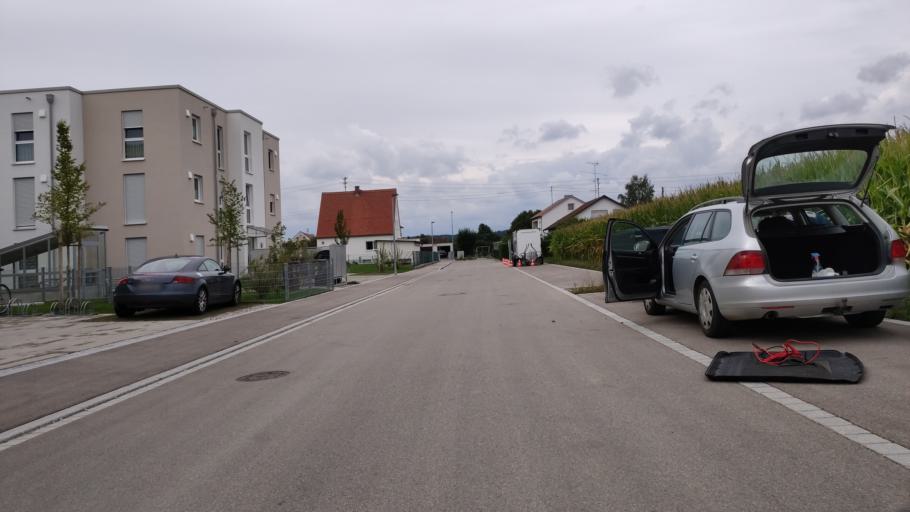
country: DE
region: Bavaria
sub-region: Swabia
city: Wehringen
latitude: 48.2459
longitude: 10.8048
